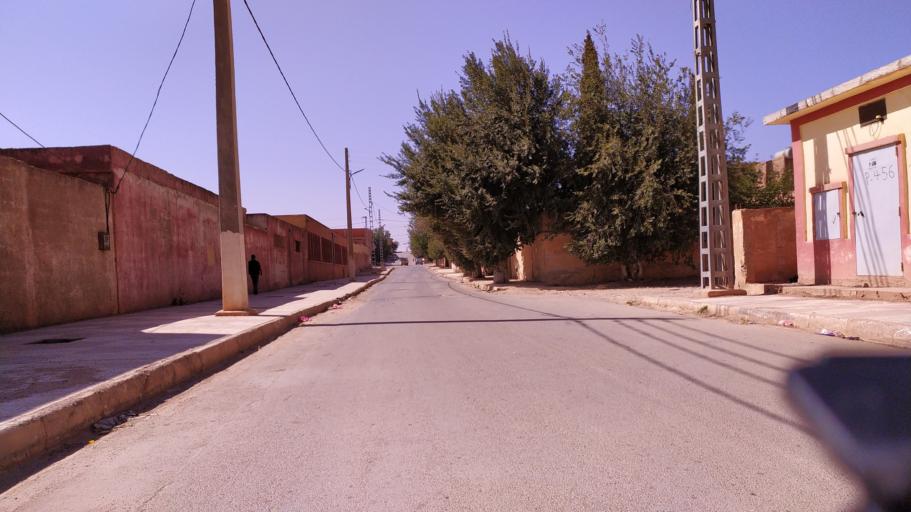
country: DZ
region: Tiaret
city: Frenda
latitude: 34.8939
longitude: 1.2426
